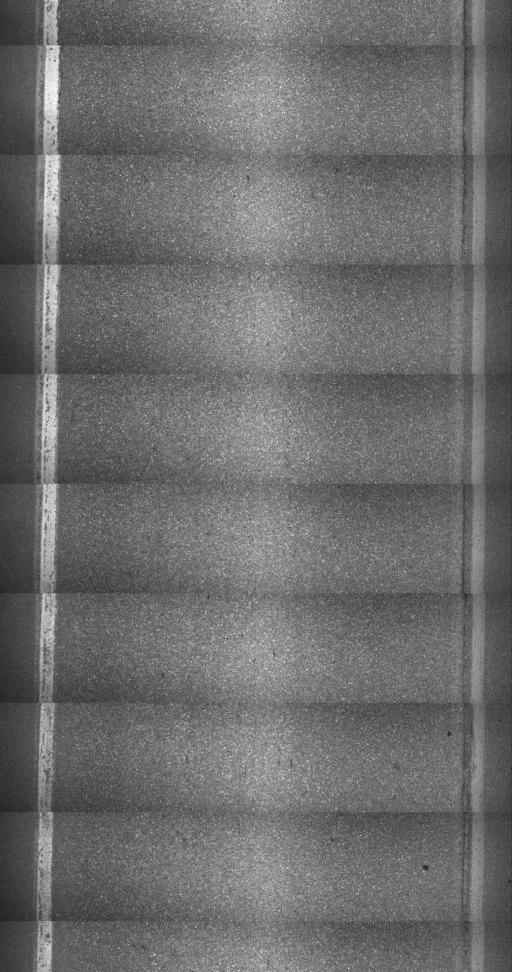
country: US
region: Vermont
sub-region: Lamoille County
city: Johnson
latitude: 44.6274
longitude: -72.6776
